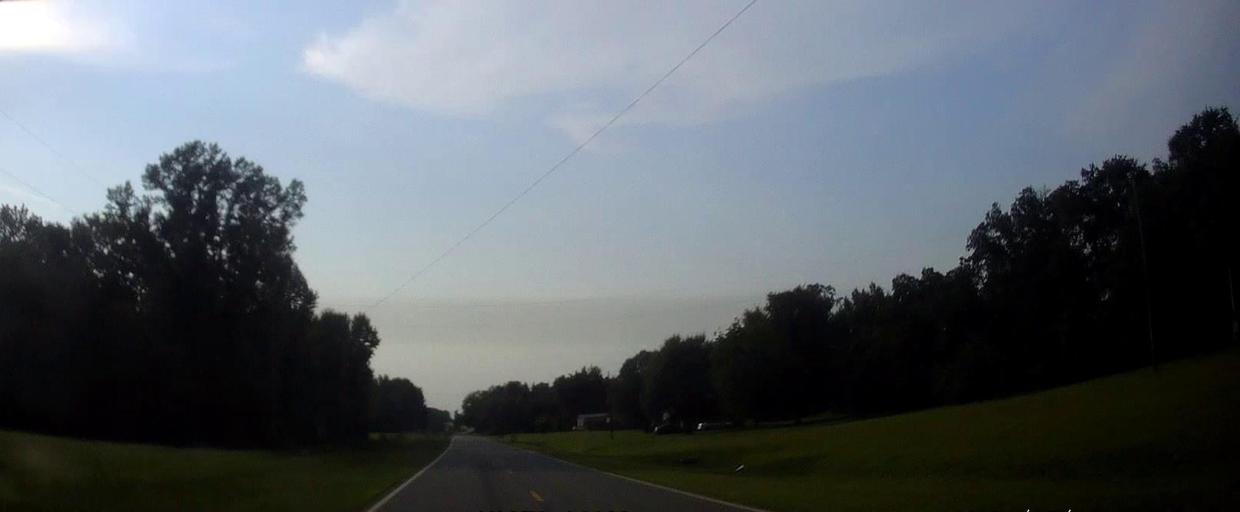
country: US
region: Georgia
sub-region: Laurens County
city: Dublin
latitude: 32.4877
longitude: -82.9770
